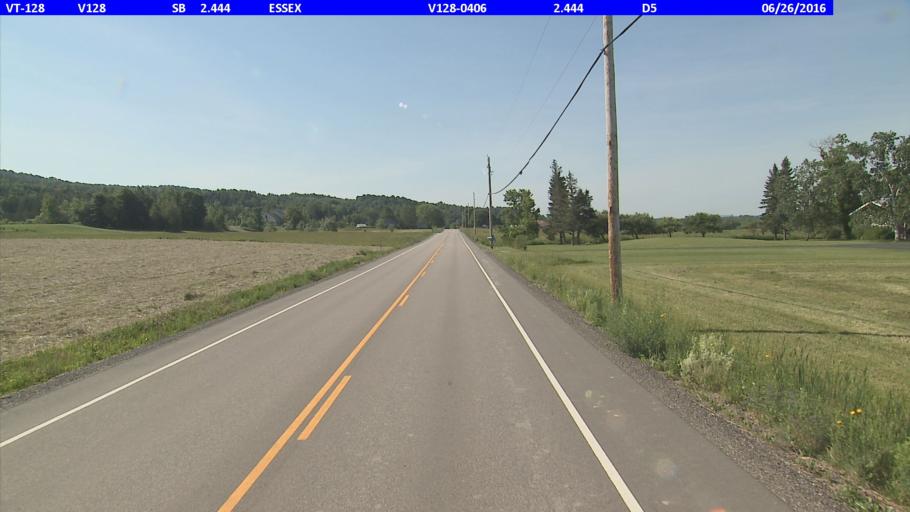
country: US
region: Vermont
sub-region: Chittenden County
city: Jericho
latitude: 44.5329
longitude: -73.0313
